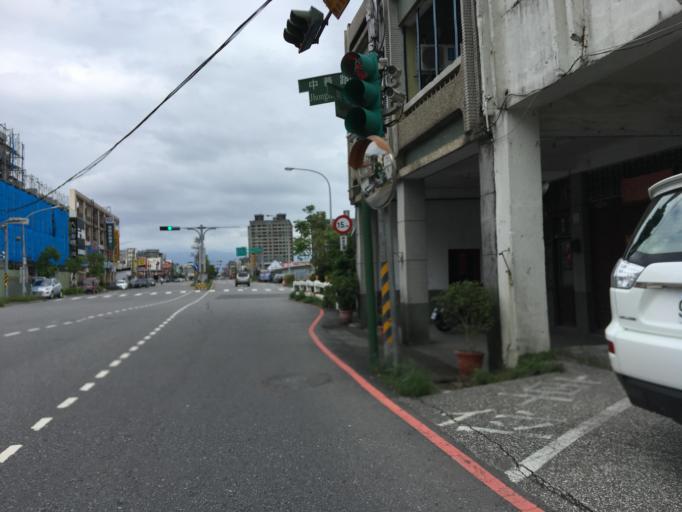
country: TW
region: Taiwan
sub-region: Yilan
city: Yilan
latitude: 24.6856
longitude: 121.7710
